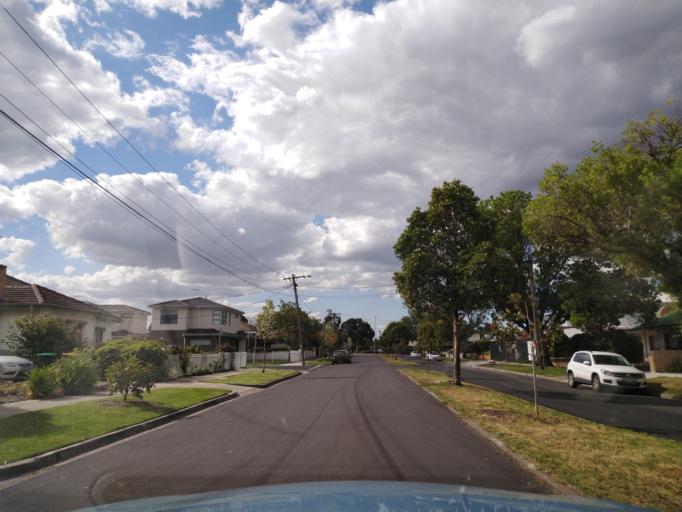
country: AU
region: Victoria
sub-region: Hobsons Bay
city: South Kingsville
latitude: -37.8421
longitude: 144.8641
